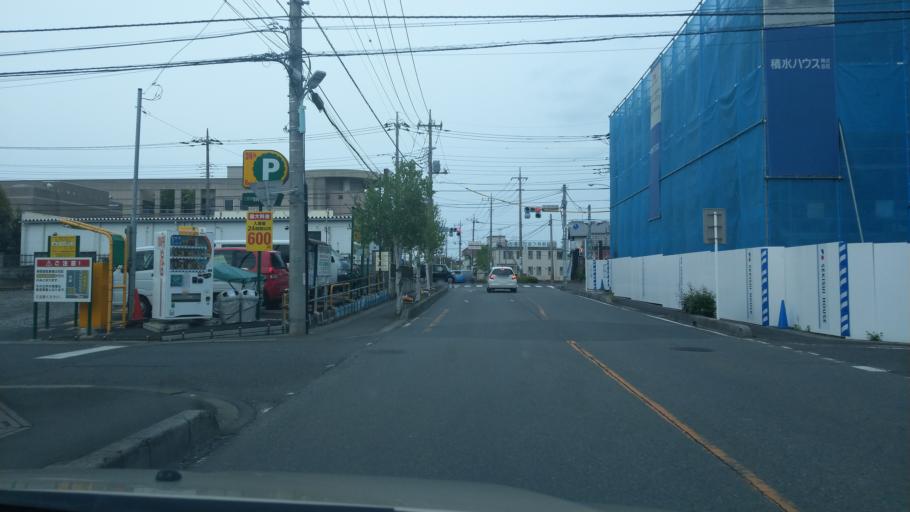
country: JP
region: Saitama
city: Ageoshimo
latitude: 35.9579
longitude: 139.6000
